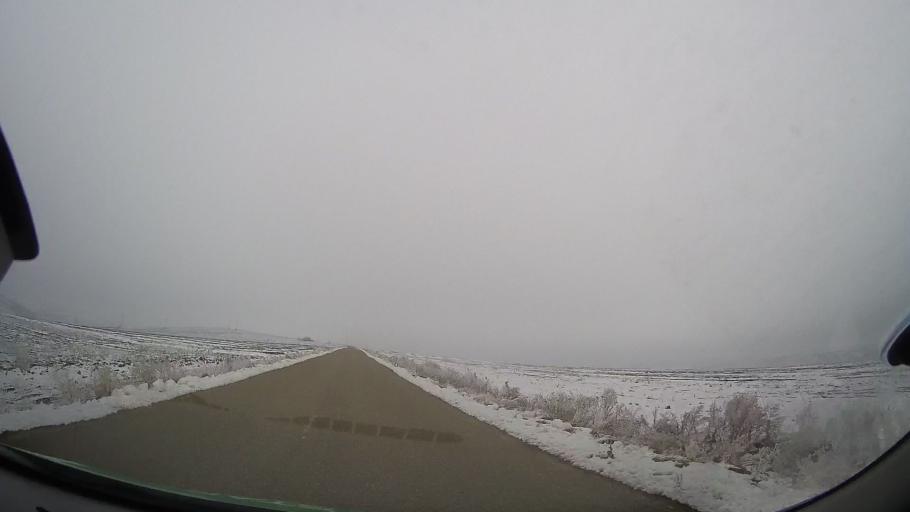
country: RO
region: Vaslui
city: Coroiesti
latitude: 46.2261
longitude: 27.4784
